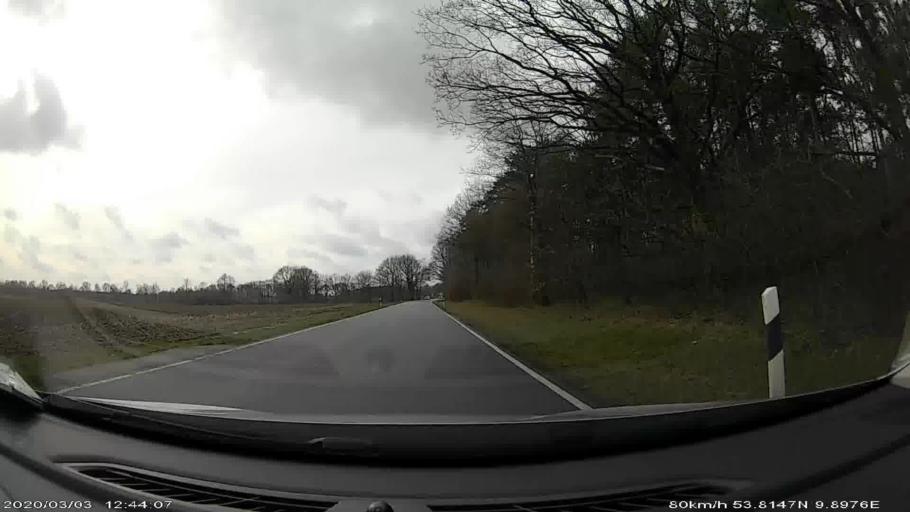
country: DE
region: Schleswig-Holstein
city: Alveslohe
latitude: 53.8137
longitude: 9.8950
